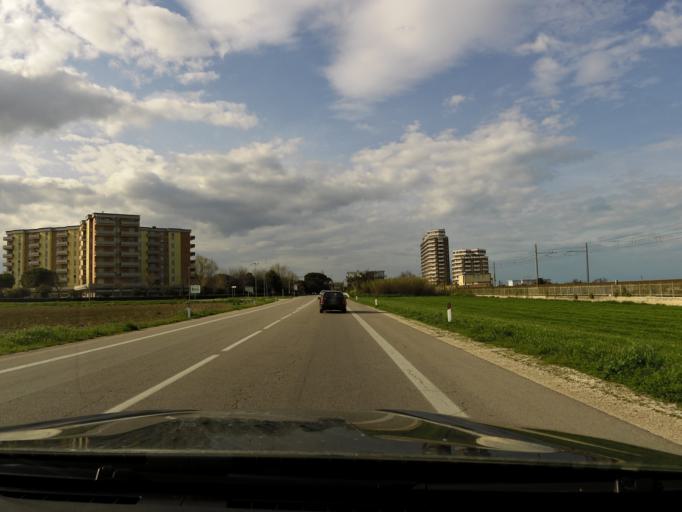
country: IT
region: The Marches
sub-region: Provincia di Macerata
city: Porto Potenza Picena
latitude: 43.3466
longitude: 13.7032
